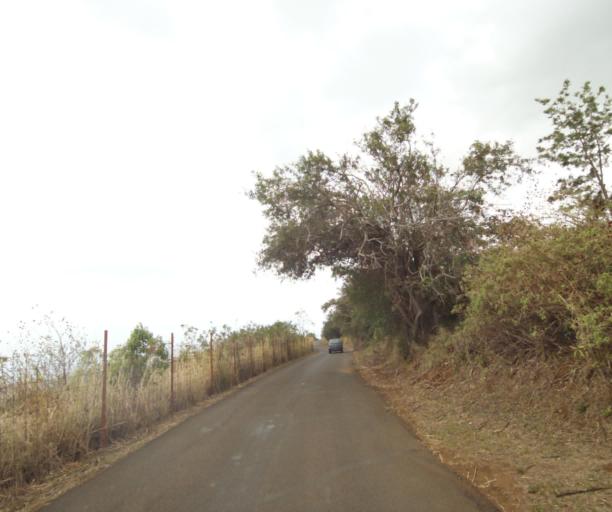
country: RE
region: Reunion
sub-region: Reunion
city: Saint-Paul
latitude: -21.0276
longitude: 55.3010
